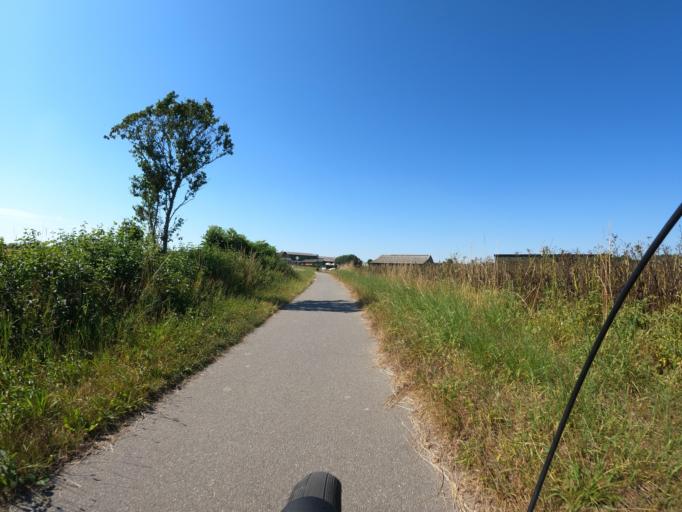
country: DE
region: Schleswig-Holstein
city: Steinberg
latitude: 54.7754
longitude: 9.7741
